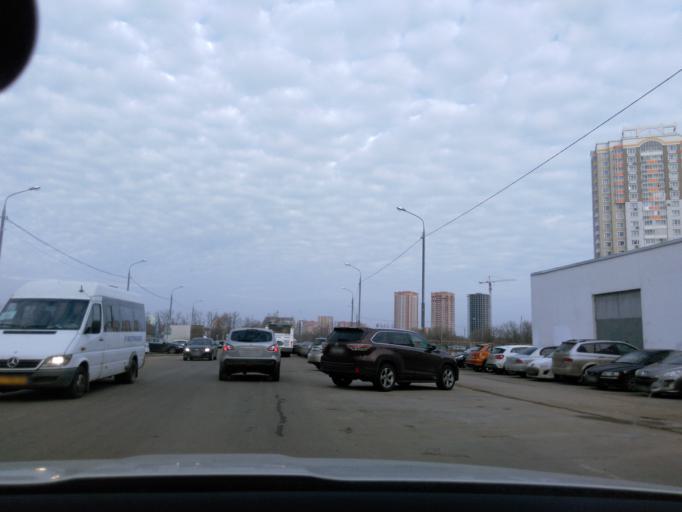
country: RU
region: Moskovskaya
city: Levoberezhnaya
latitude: 55.8991
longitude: 37.4760
